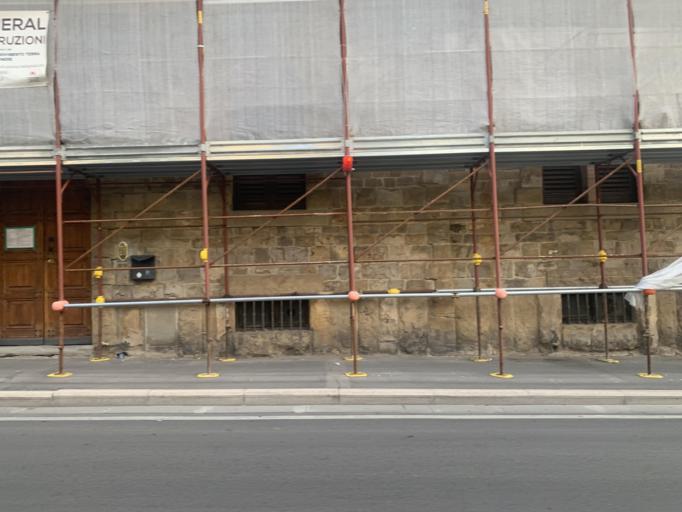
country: IT
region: Tuscany
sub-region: Province of Florence
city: Florence
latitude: 43.7887
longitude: 11.2491
